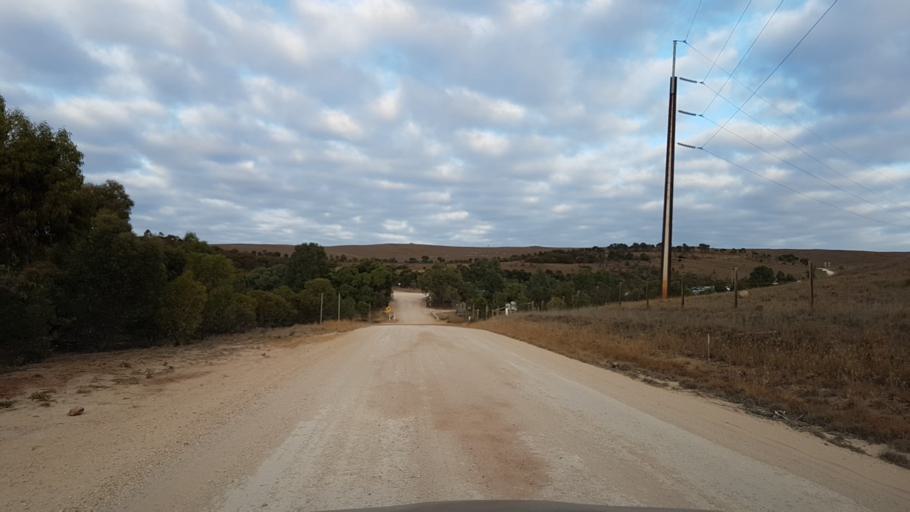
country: AU
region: South Australia
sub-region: Mount Barker
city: Callington
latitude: -35.1012
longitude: 139.0038
